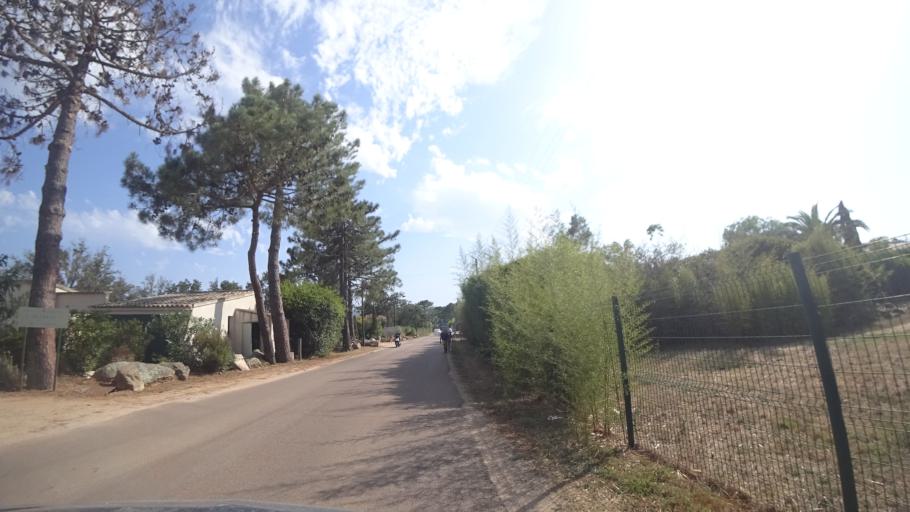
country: FR
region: Corsica
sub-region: Departement de la Corse-du-Sud
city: Porto-Vecchio
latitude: 41.6253
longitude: 9.3369
